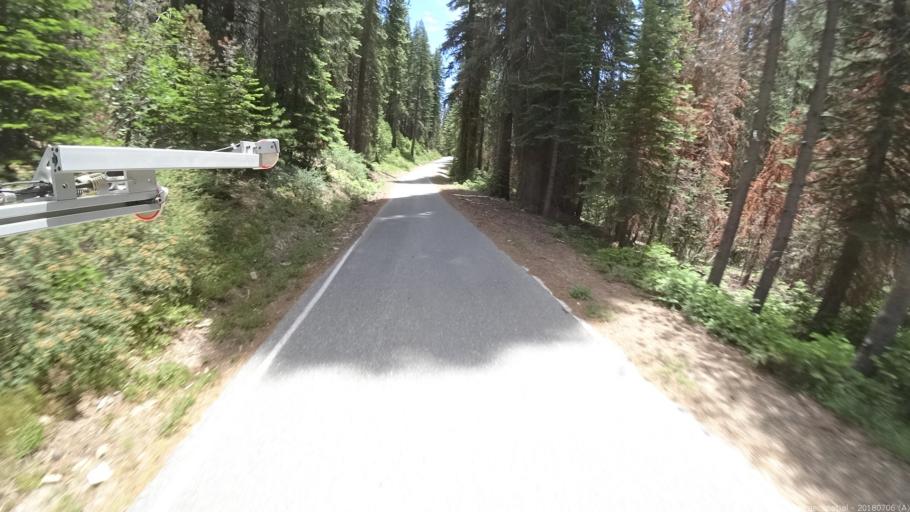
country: US
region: California
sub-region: Madera County
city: Oakhurst
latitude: 37.4274
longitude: -119.4296
